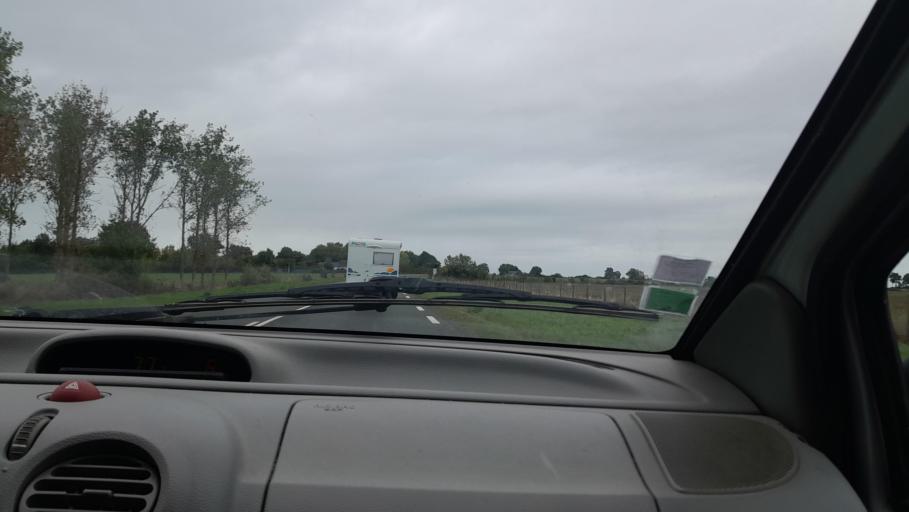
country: FR
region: Pays de la Loire
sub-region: Departement de la Loire-Atlantique
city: Mesanger
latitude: 47.4642
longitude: -1.1782
